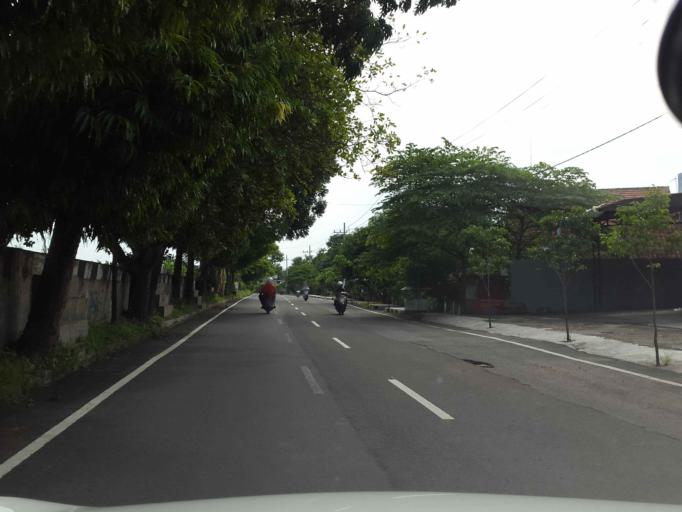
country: ID
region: East Java
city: Mojokerto
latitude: -7.4572
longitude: 112.4398
